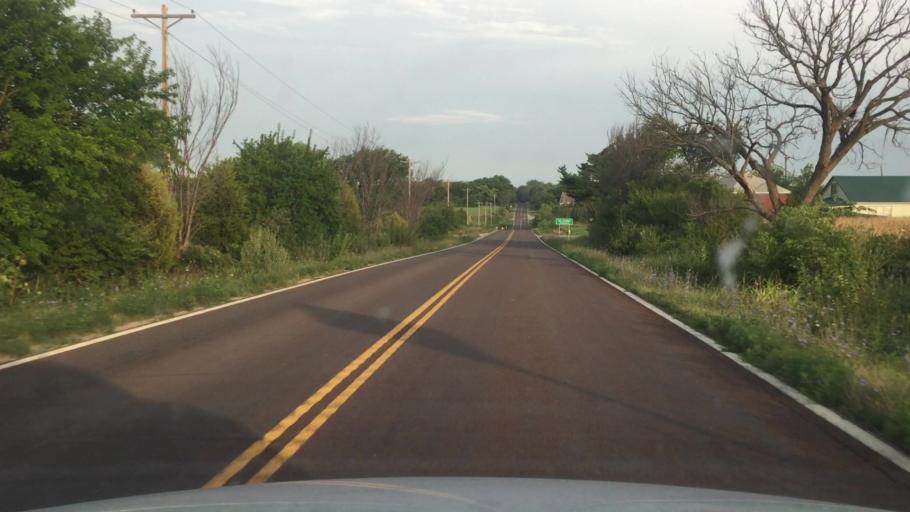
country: US
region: Kansas
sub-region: Shawnee County
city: Topeka
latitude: 39.0114
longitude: -95.4774
